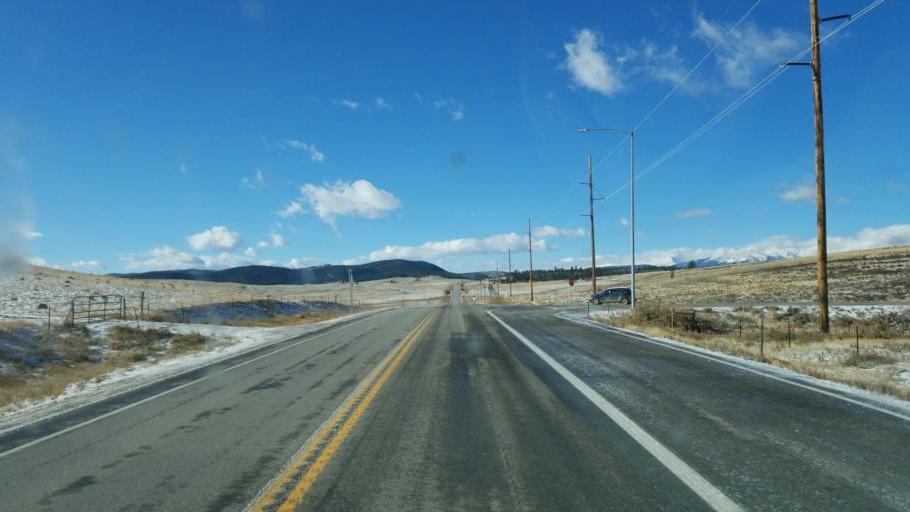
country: US
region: Colorado
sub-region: Park County
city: Fairplay
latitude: 39.3110
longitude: -105.8860
